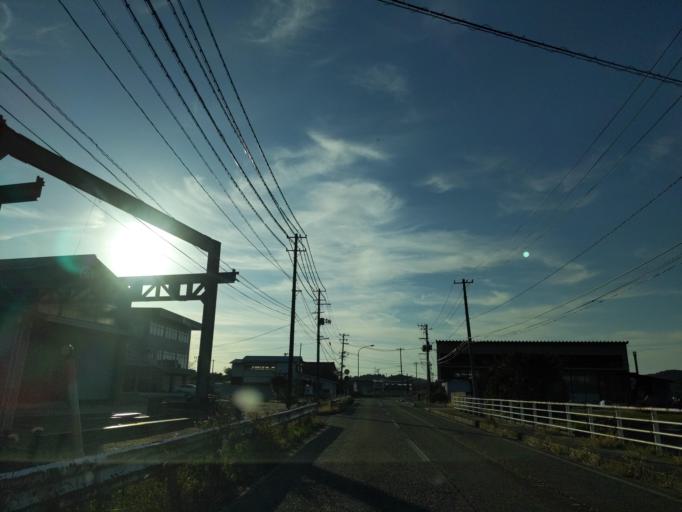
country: JP
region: Niigata
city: Yoshida-kasugacho
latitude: 37.5806
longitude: 138.7804
